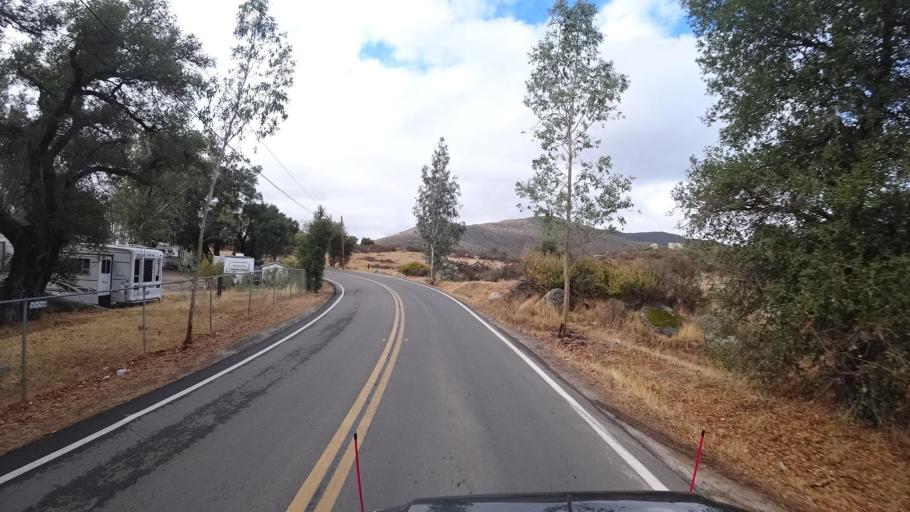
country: MX
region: Baja California
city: Tecate
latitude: 32.6256
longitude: -116.6132
